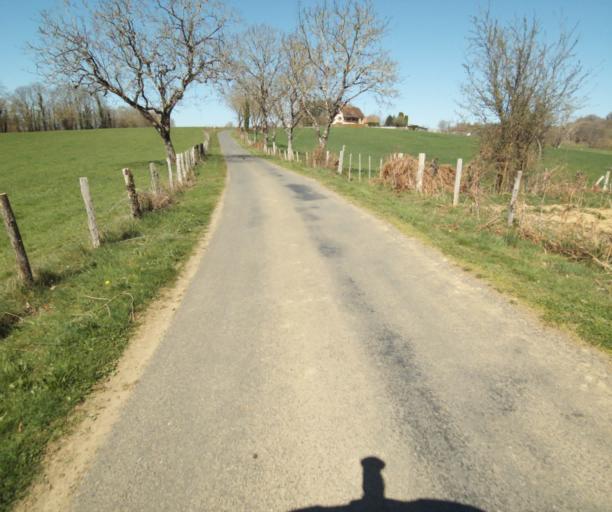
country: FR
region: Limousin
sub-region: Departement de la Correze
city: Saint-Clement
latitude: 45.3321
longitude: 1.7084
